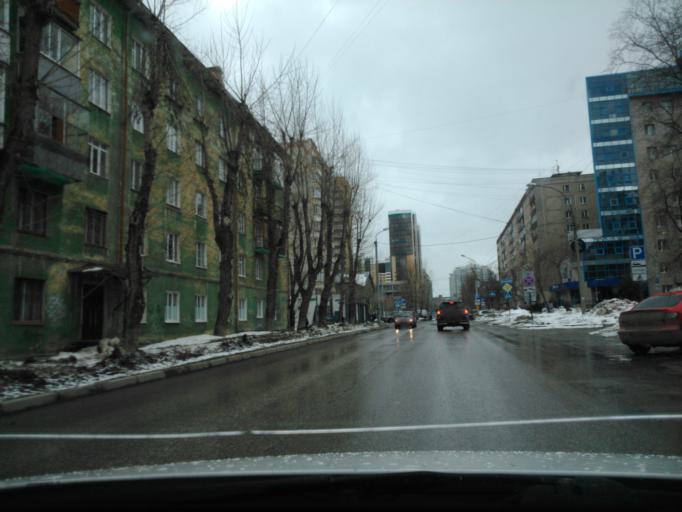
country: RU
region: Perm
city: Perm
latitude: 58.0045
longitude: 56.2628
